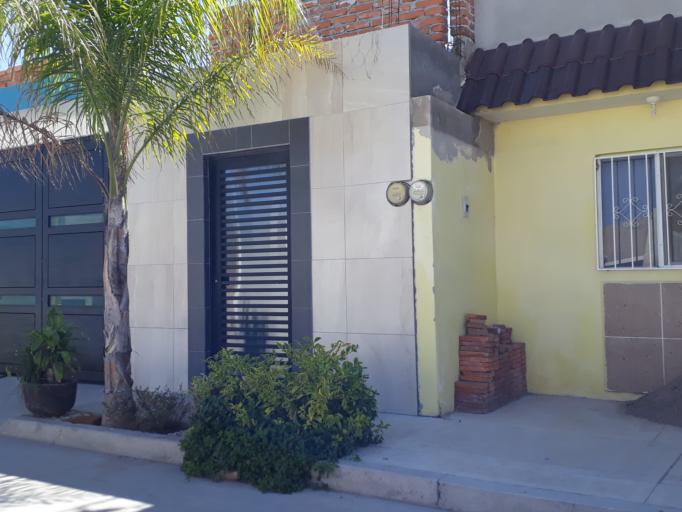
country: MX
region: Aguascalientes
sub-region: Aguascalientes
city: San Sebastian [Fraccionamiento]
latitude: 21.8364
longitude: -102.2959
